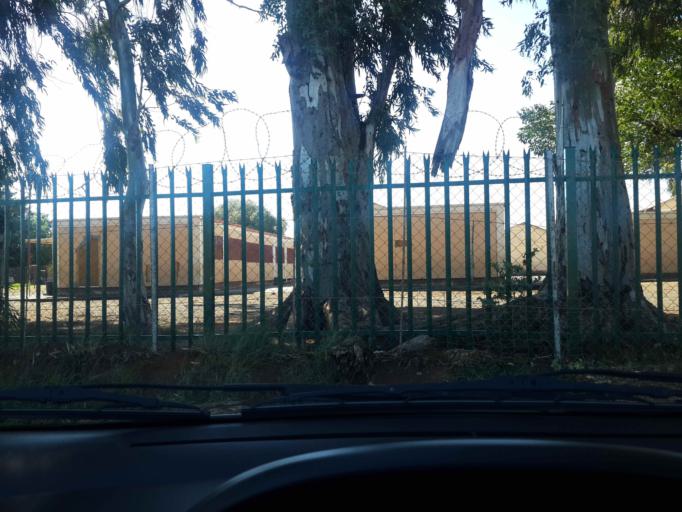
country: ZA
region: Northern Cape
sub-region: Siyanda District Municipality
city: Danielskuil
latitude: -28.1902
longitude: 23.5374
